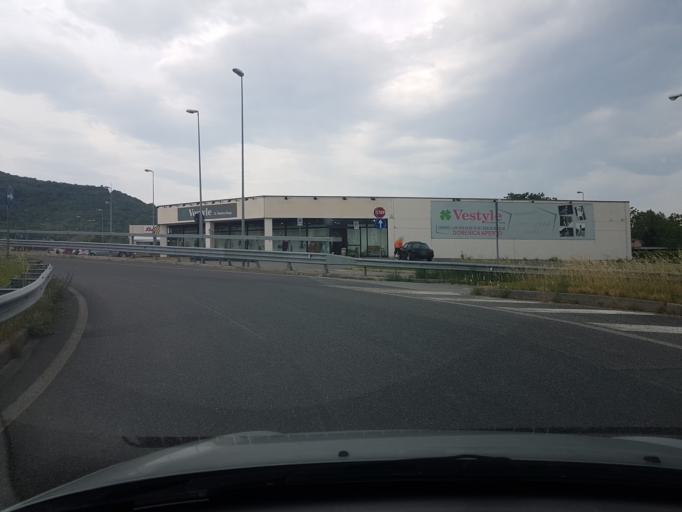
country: SI
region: Koper-Capodistria
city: Spodnje Skofije
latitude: 45.5877
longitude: 13.8033
